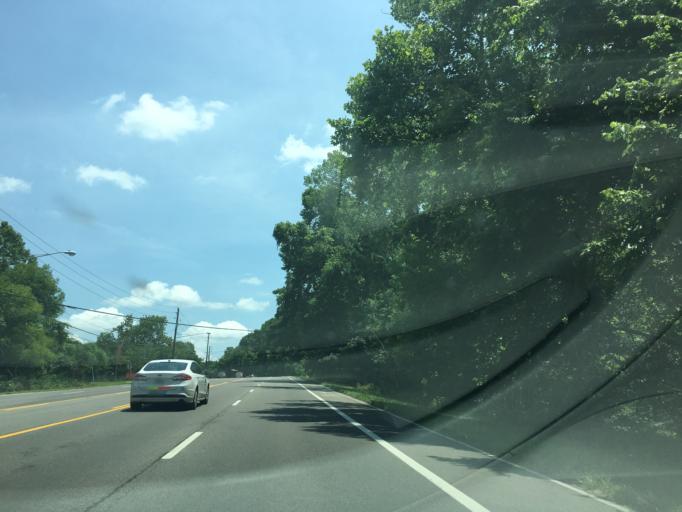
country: US
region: Tennessee
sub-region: Davidson County
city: Belle Meade
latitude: 36.0799
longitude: -86.9027
